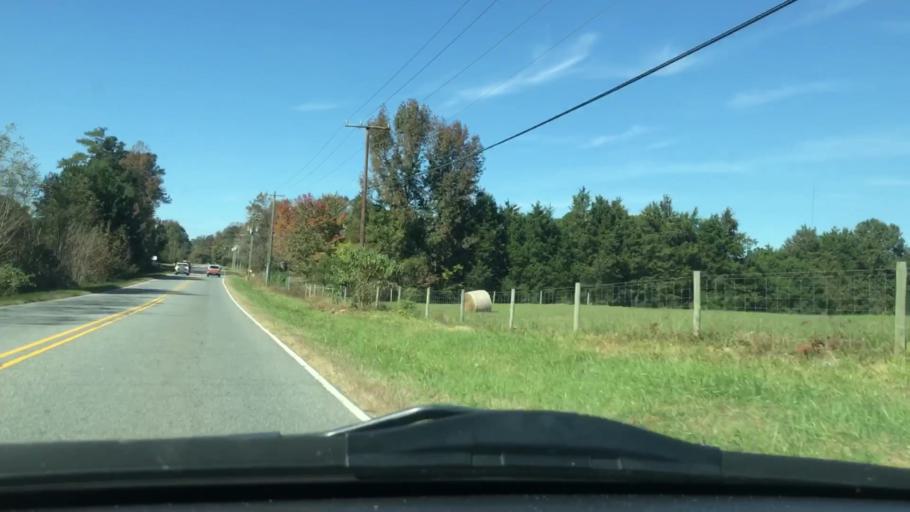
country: US
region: North Carolina
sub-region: Randolph County
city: Randleman
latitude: 35.8086
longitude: -79.8326
